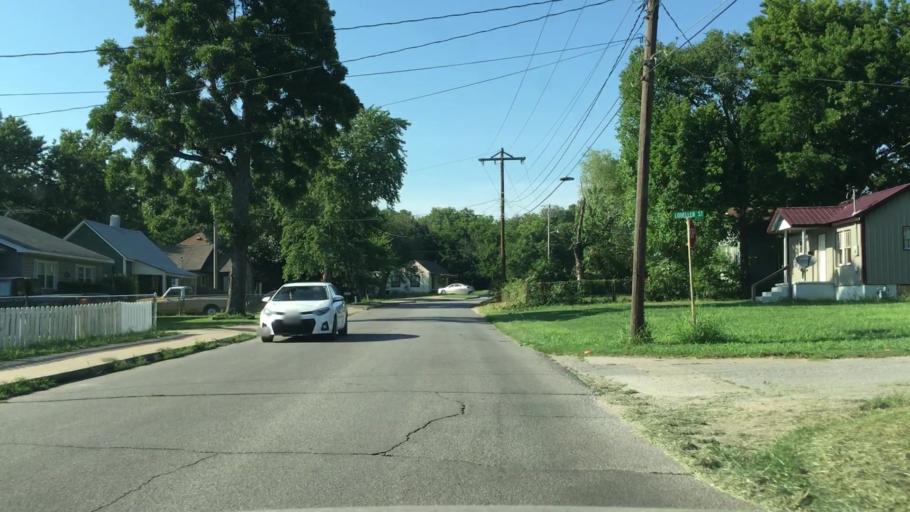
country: US
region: Oklahoma
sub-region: Cherokee County
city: Tahlequah
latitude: 35.9062
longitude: -94.9757
